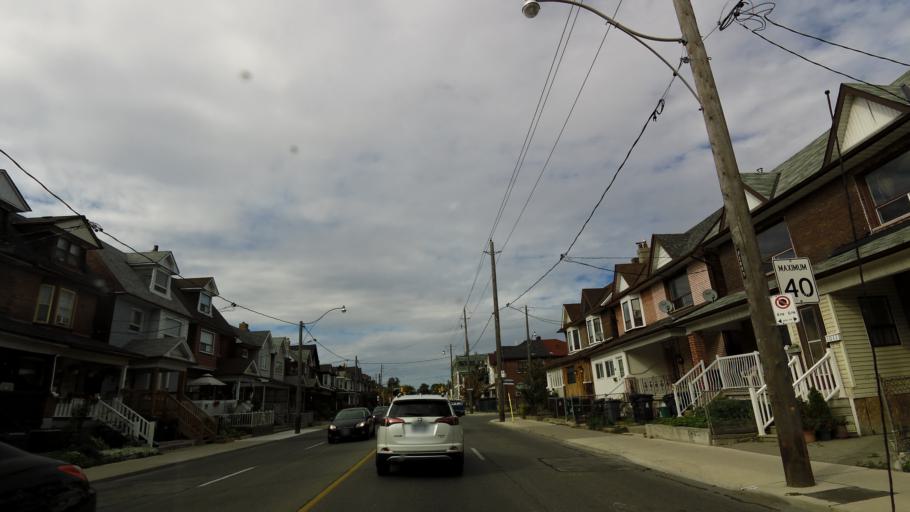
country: CA
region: Ontario
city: Toronto
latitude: 43.6688
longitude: -79.4286
